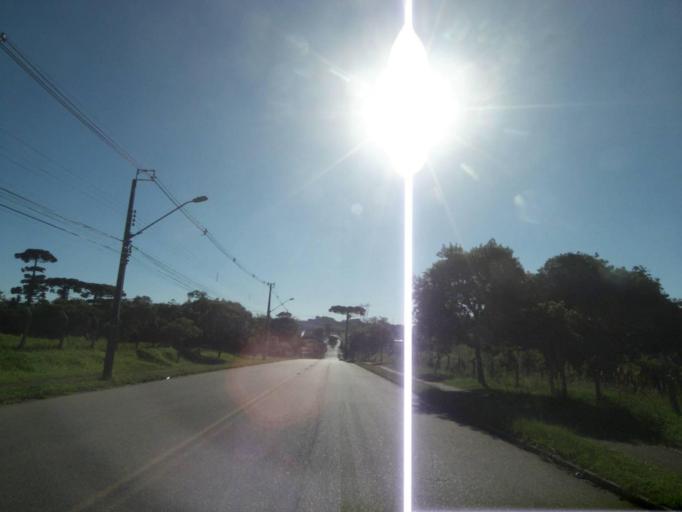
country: BR
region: Parana
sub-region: Curitiba
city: Curitiba
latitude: -25.4643
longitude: -49.3491
